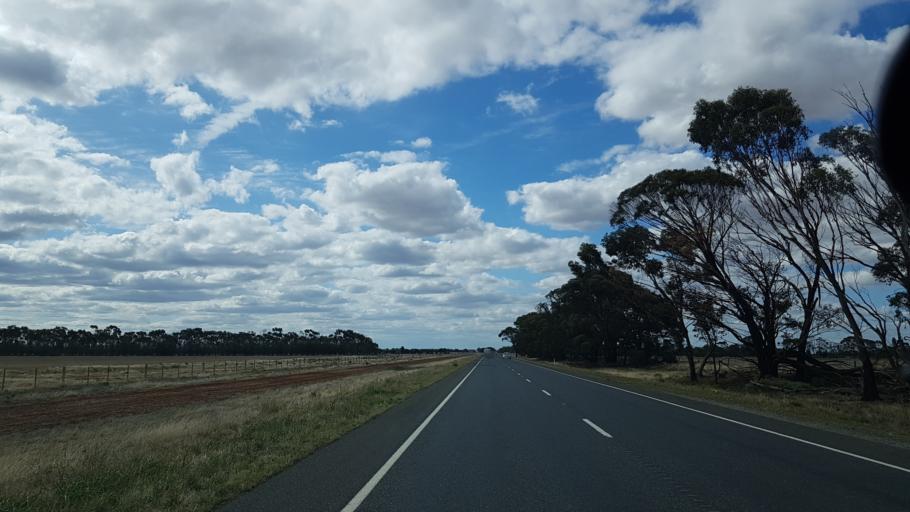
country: AU
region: Victoria
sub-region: Greater Bendigo
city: Long Gully
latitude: -36.0473
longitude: 143.9482
